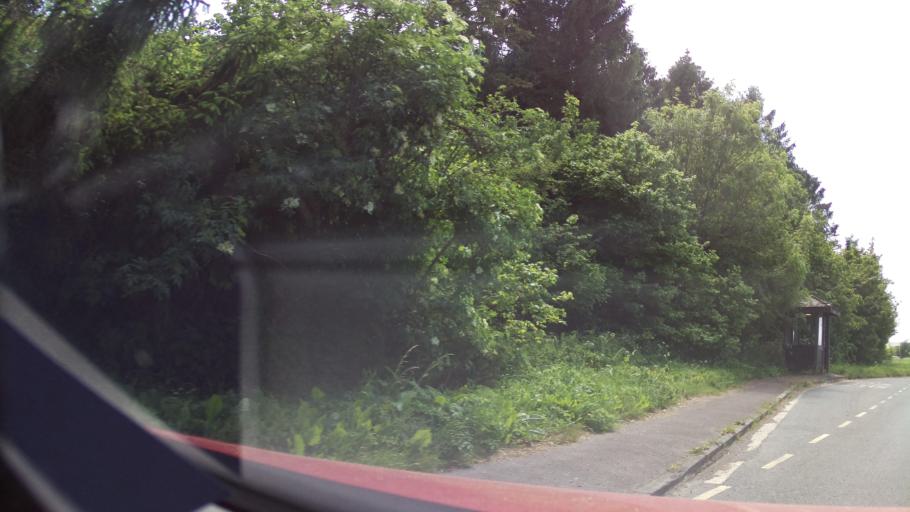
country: GB
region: England
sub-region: Wiltshire
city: Avebury
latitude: 51.4185
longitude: -1.8766
